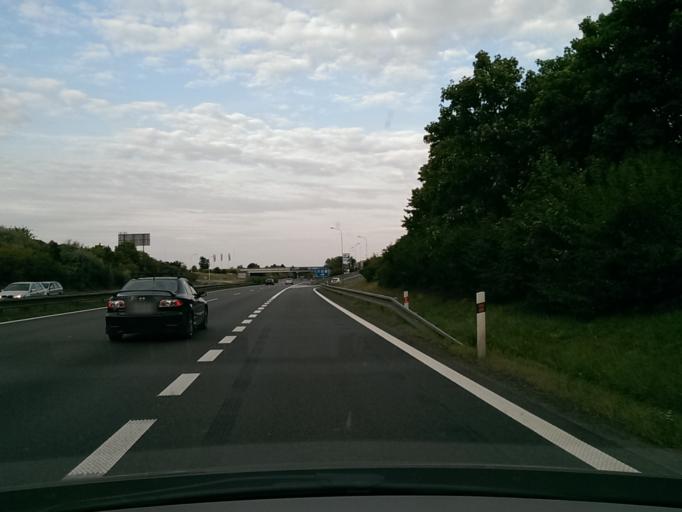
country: CZ
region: South Moravian
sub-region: Mesto Brno
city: Brno
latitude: 49.1631
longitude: 16.6573
